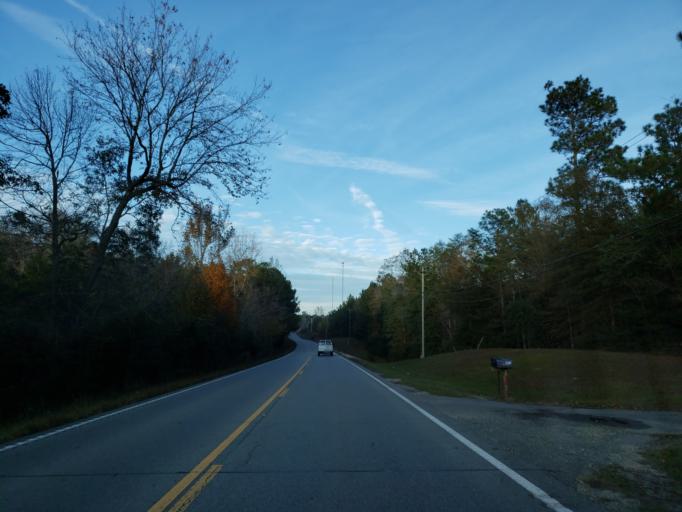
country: US
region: Mississippi
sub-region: Lamar County
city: West Hattiesburg
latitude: 31.2408
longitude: -89.3476
